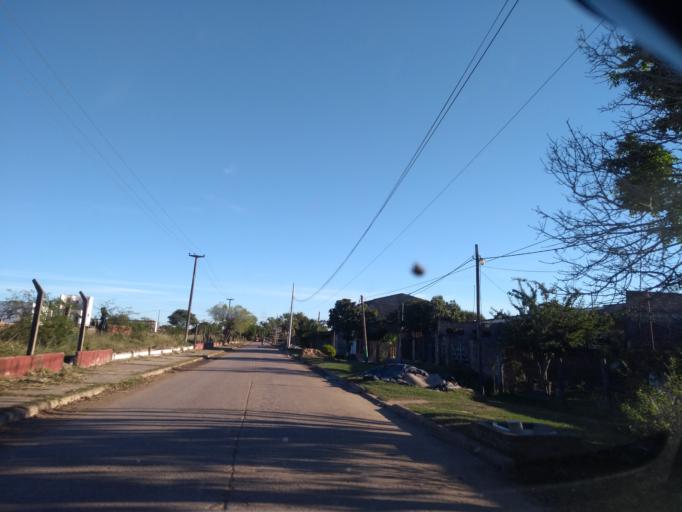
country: AR
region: Chaco
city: Puerto Vilelas
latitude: -27.4993
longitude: -58.9329
